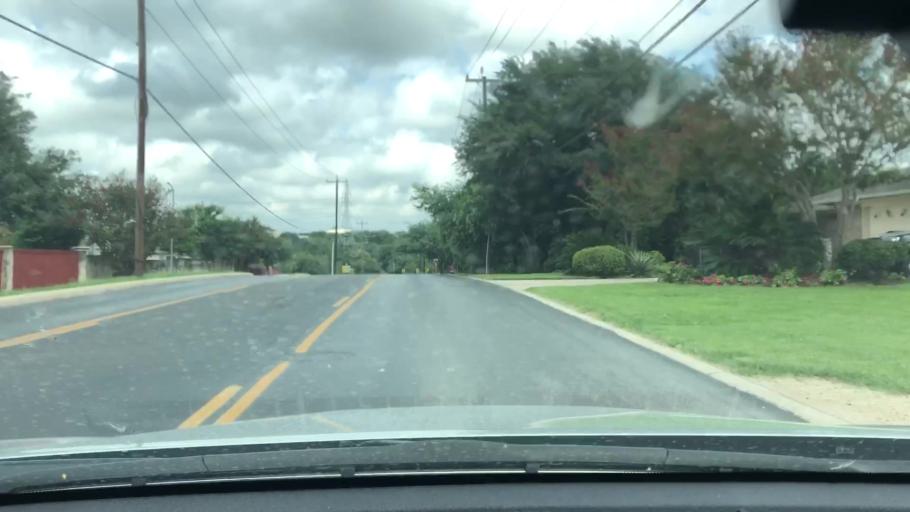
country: US
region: Texas
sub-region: Bexar County
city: Windcrest
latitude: 29.5285
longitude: -98.3693
